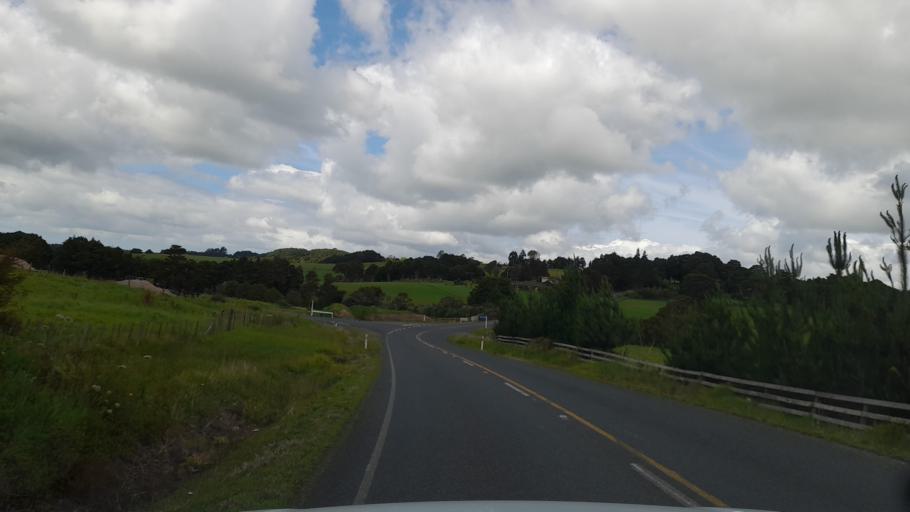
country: NZ
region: Northland
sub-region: Whangarei
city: Maungatapere
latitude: -35.6524
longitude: 174.1500
